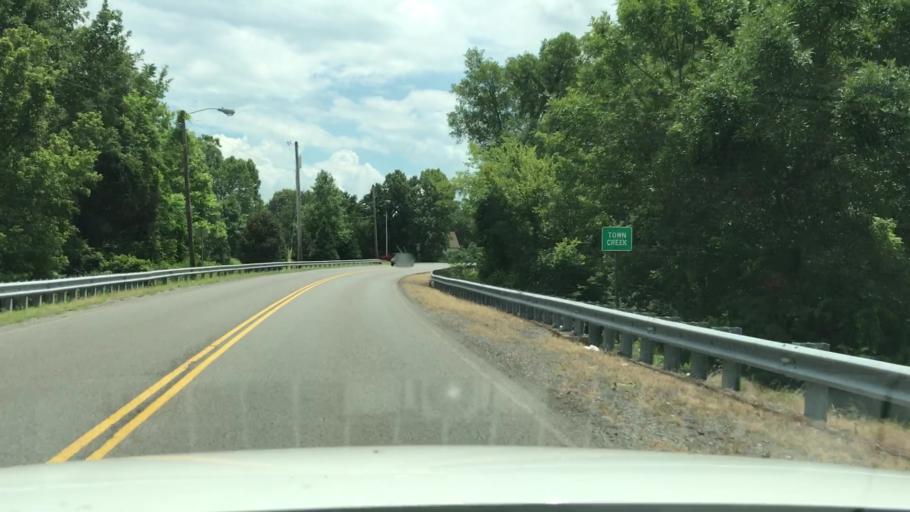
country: US
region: Tennessee
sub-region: Sumner County
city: Gallatin
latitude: 36.3653
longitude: -86.4663
